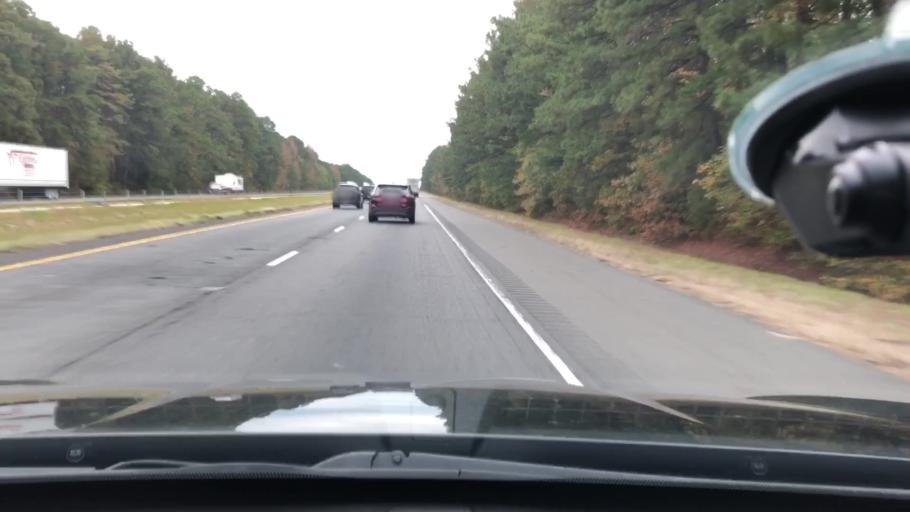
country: US
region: Arkansas
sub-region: Clark County
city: Gurdon
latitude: 34.0395
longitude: -93.1410
